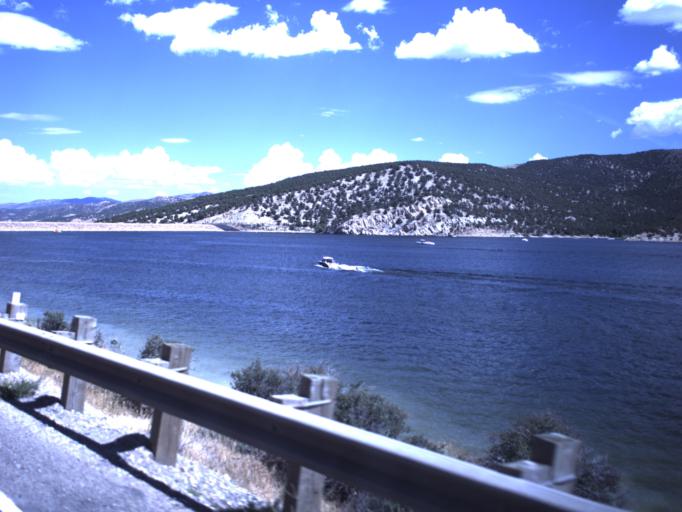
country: US
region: Utah
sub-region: Summit County
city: Oakley
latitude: 40.7816
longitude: -111.4089
